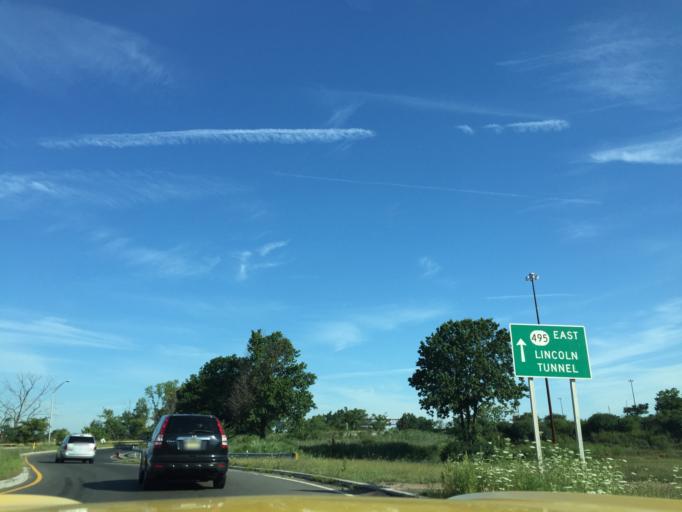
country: US
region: New Jersey
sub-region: Hudson County
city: Secaucus
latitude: 40.7759
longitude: -74.0458
